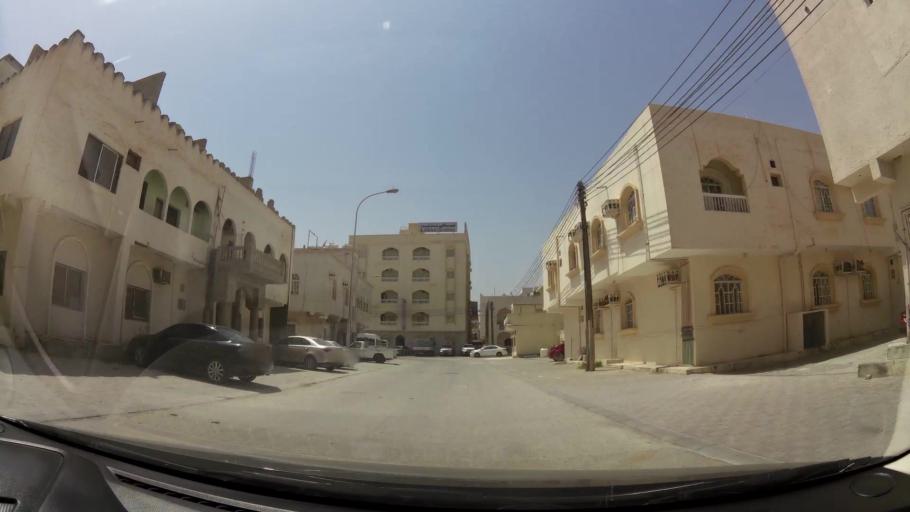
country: OM
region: Zufar
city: Salalah
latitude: 17.0163
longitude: 54.0845
